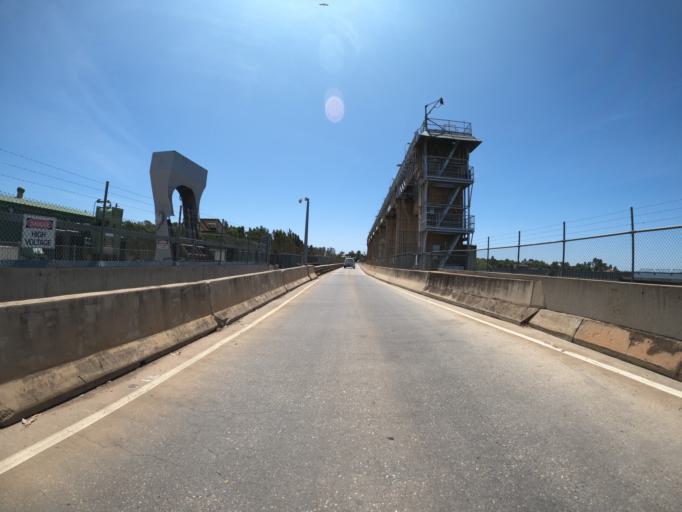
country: AU
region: Victoria
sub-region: Moira
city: Yarrawonga
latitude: -36.0096
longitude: 145.9996
